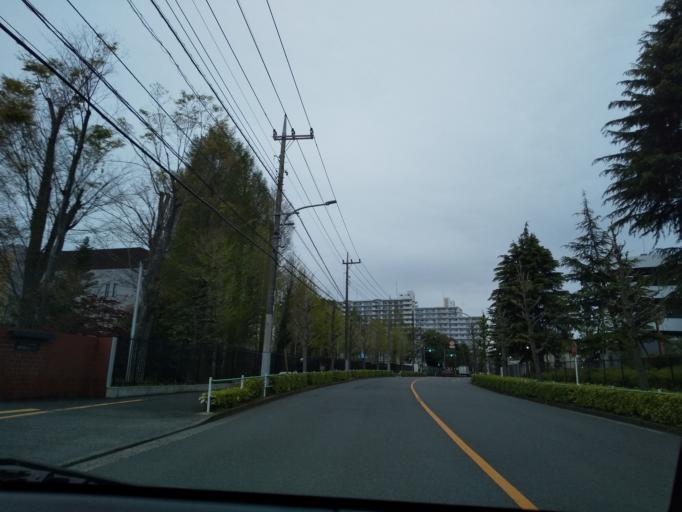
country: JP
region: Tokyo
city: Hino
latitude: 35.6539
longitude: 139.3681
